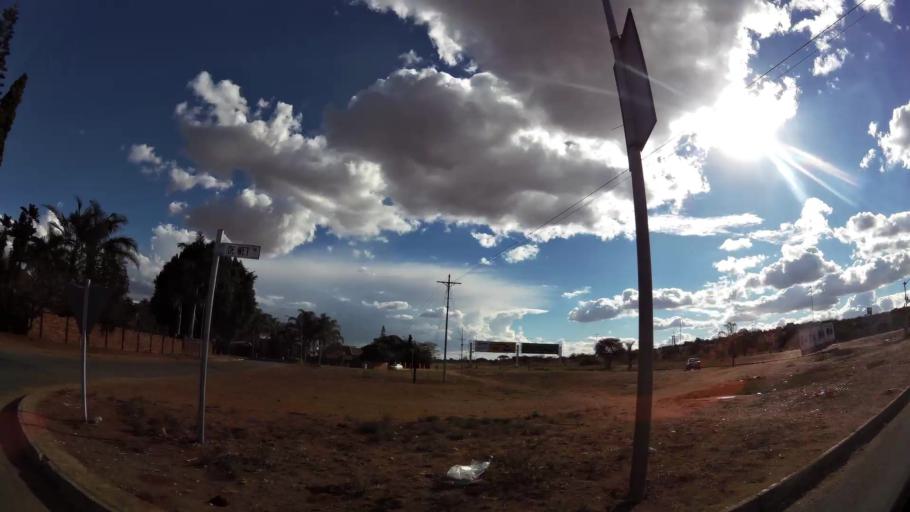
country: ZA
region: Limpopo
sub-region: Capricorn District Municipality
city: Polokwane
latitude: -23.9007
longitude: 29.4986
